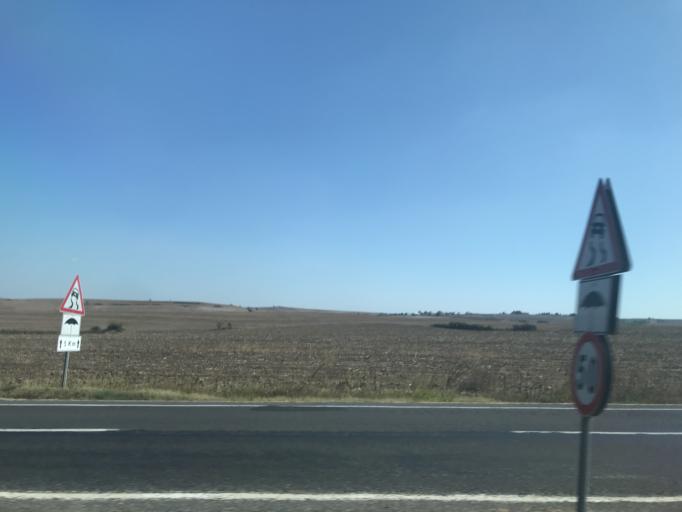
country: TR
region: Tekirdag
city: Muratli
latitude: 41.0948
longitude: 27.4926
